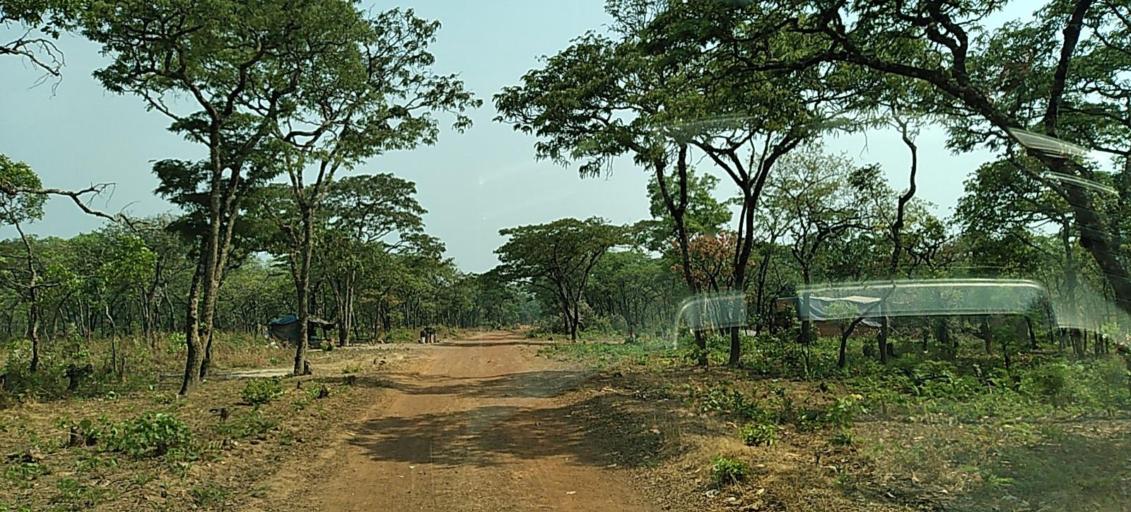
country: ZM
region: North-Western
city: Kansanshi
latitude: -12.0792
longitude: 26.8880
